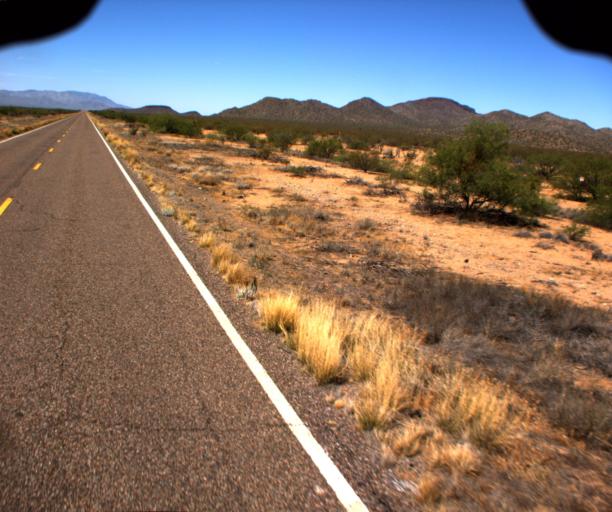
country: US
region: Arizona
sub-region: Yavapai County
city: Congress
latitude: 34.0459
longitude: -113.0642
